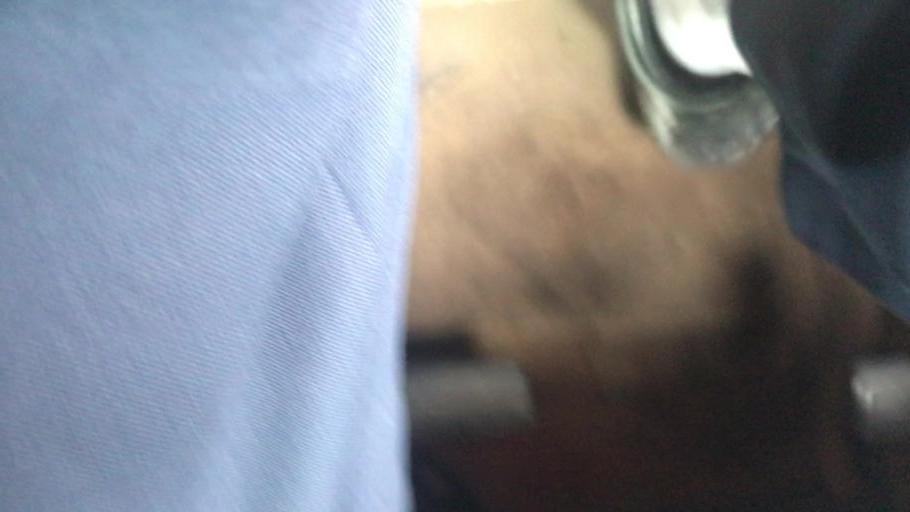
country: US
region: Tennessee
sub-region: Shelby County
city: Germantown
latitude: 35.0621
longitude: -89.8963
